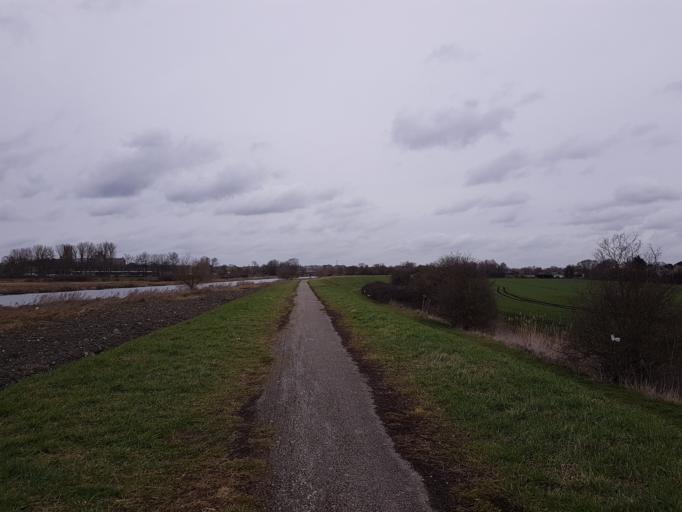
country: GB
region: England
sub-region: Cambridgeshire
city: Ely
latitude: 52.3852
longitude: 0.2673
